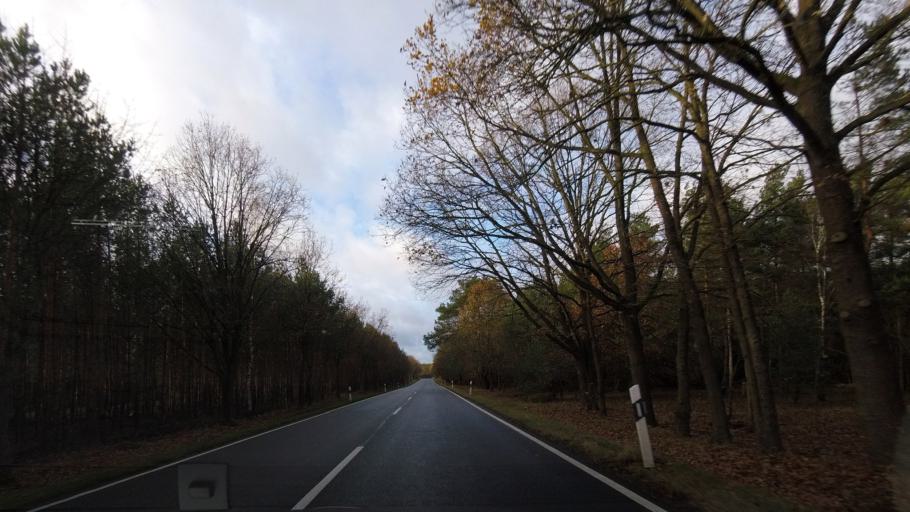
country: DE
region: Brandenburg
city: Treuenbrietzen
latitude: 52.0398
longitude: 12.9296
